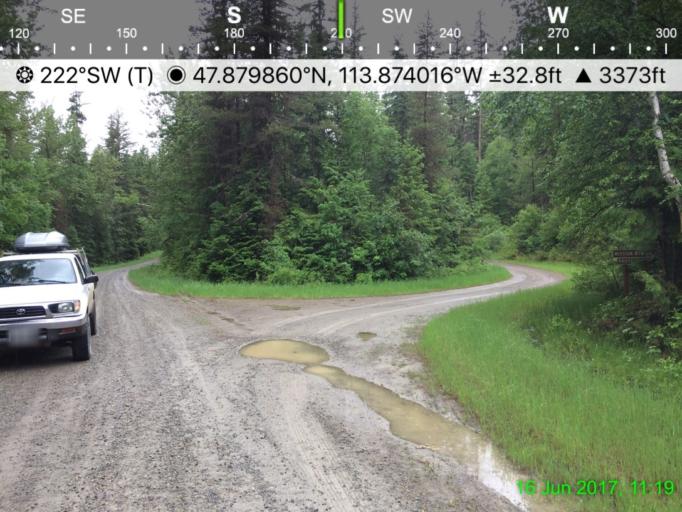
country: US
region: Montana
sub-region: Flathead County
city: Bigfork
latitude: 47.8799
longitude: -113.8740
